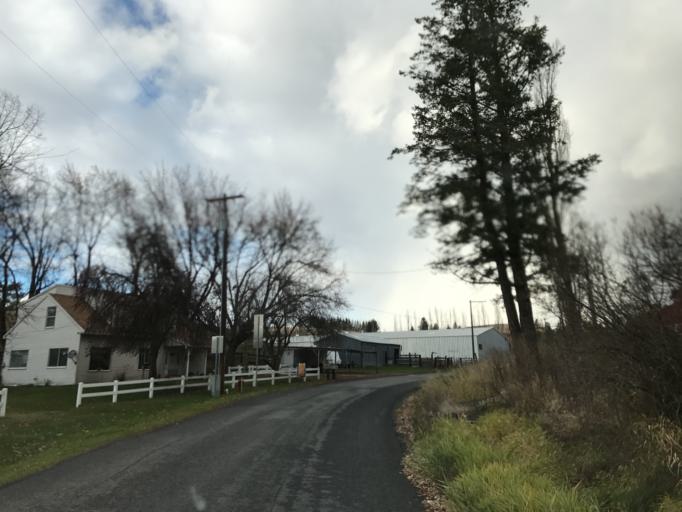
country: US
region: Idaho
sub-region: Latah County
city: Moscow
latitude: 46.7517
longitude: -116.9958
